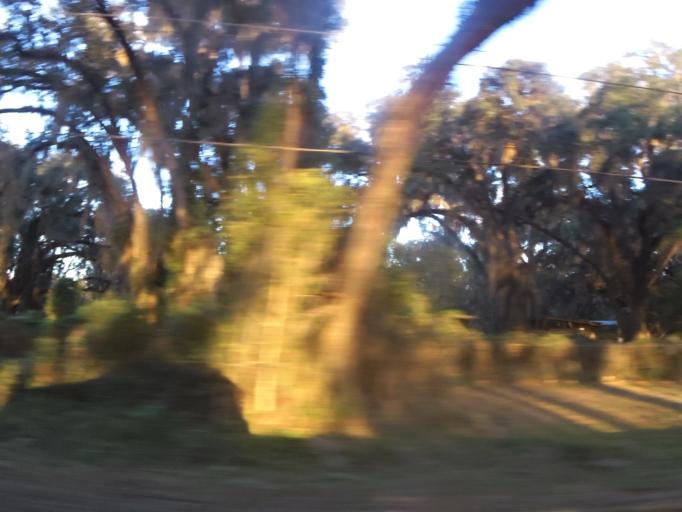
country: US
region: Florida
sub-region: Clay County
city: Green Cove Springs
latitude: 29.9122
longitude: -81.5918
